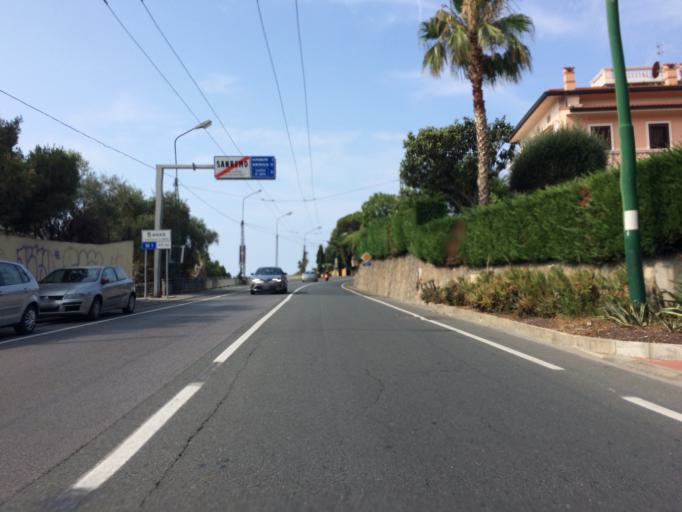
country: IT
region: Liguria
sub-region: Provincia di Imperia
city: Ospedaletti
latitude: 43.8018
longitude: 7.7441
